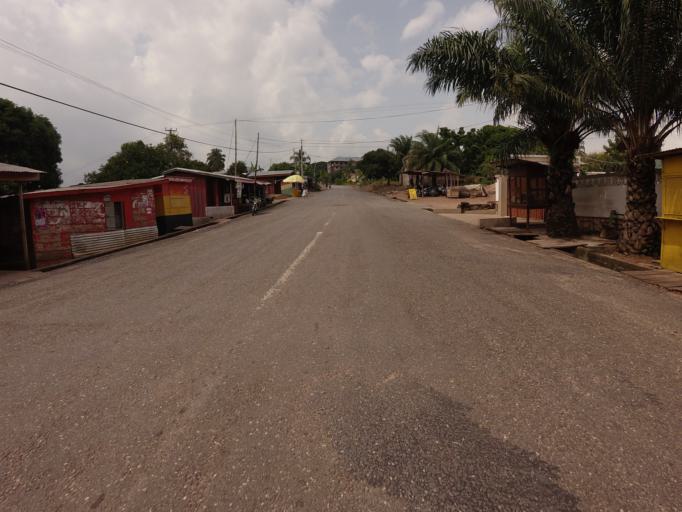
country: GH
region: Volta
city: Ho
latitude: 6.6162
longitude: 0.4779
